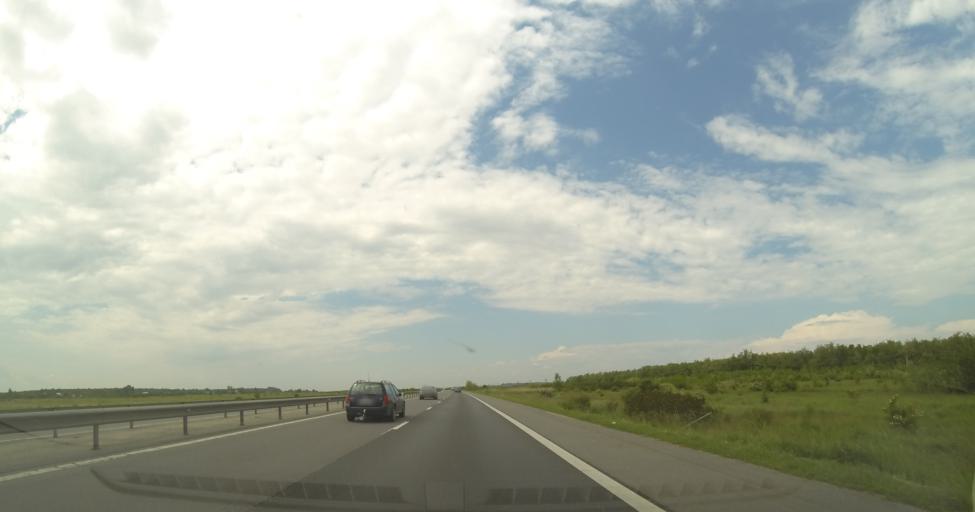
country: RO
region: Dambovita
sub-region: Comuna Mogosani
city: Zavoiu
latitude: 44.6394
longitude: 25.4014
